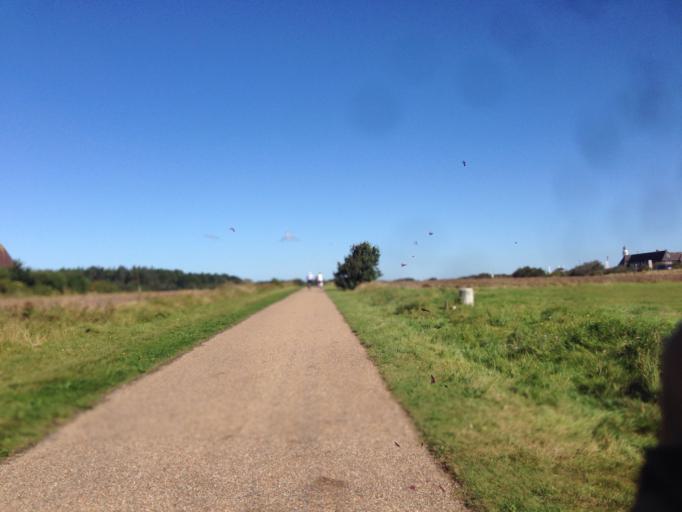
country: DE
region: Schleswig-Holstein
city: Tinnum
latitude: 54.9400
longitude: 8.3312
